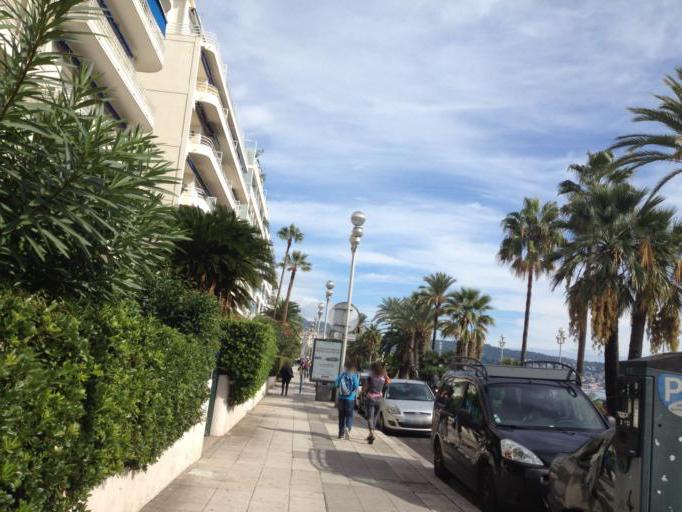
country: FR
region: Provence-Alpes-Cote d'Azur
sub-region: Departement des Alpes-Maritimes
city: Nice
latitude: 43.6914
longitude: 7.2473
